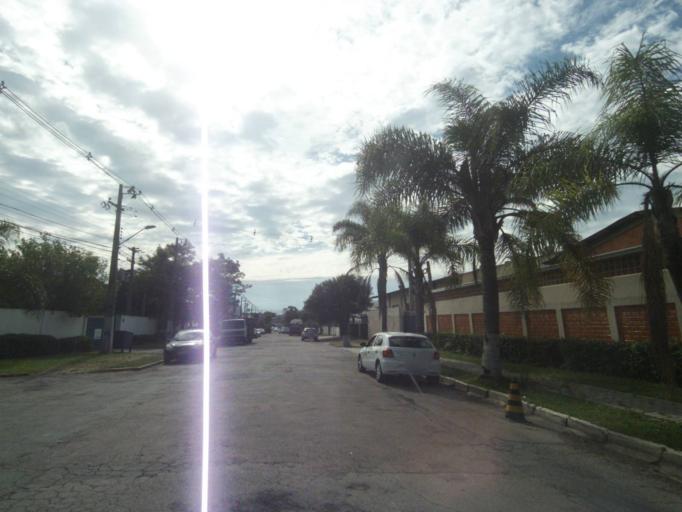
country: BR
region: Parana
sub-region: Curitiba
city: Curitiba
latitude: -25.4996
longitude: -49.3305
